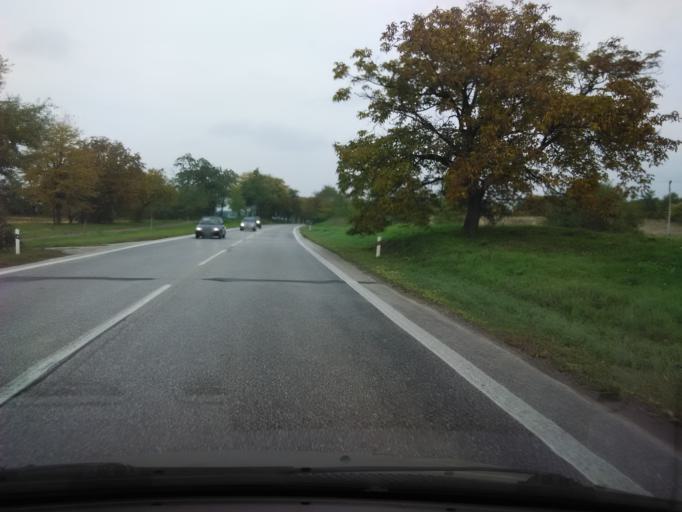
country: SK
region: Nitriansky
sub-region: Okres Komarno
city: Hurbanovo
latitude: 47.8973
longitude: 18.2025
